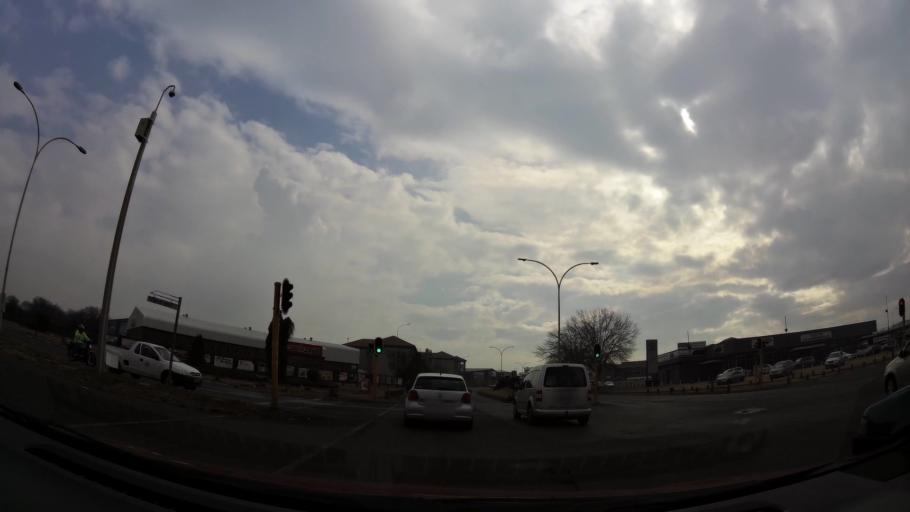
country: ZA
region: Gauteng
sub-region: Sedibeng District Municipality
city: Vanderbijlpark
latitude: -26.6980
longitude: 27.8323
